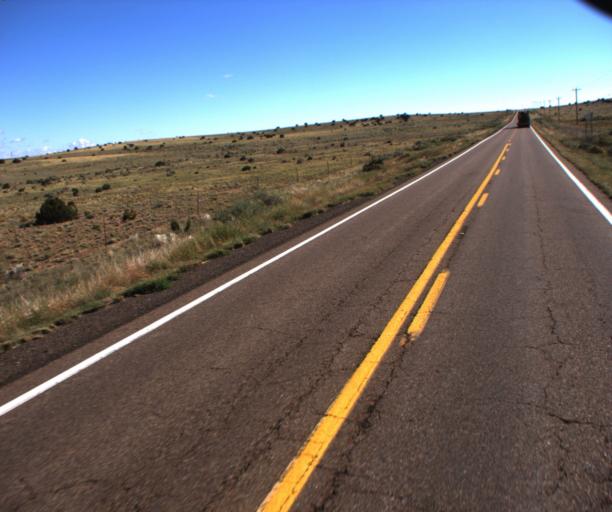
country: US
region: Arizona
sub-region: Apache County
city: Saint Johns
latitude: 34.4860
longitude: -109.5379
